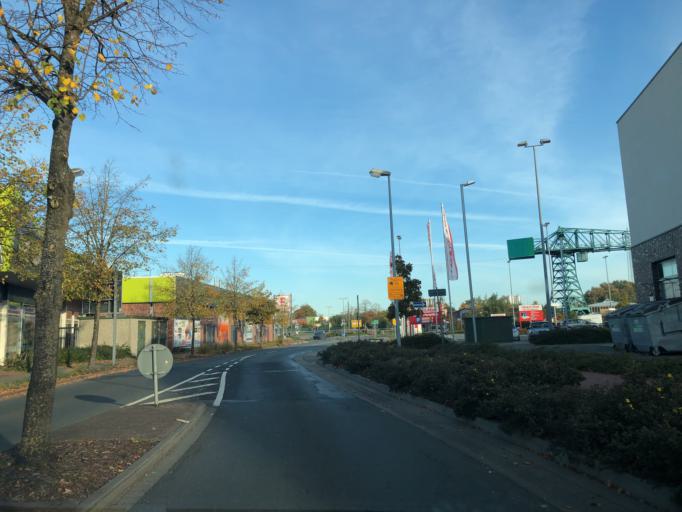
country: DE
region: Lower Saxony
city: Papenburg
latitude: 53.0847
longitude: 7.3844
